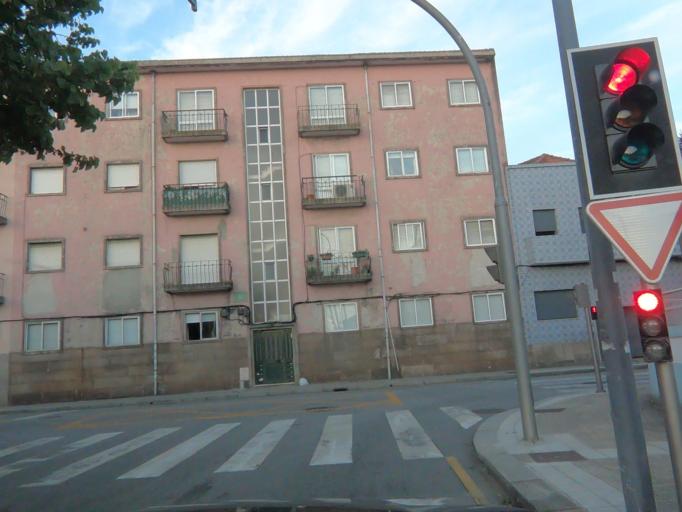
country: PT
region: Porto
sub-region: Porto
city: Porto
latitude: 41.1756
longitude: -8.6140
